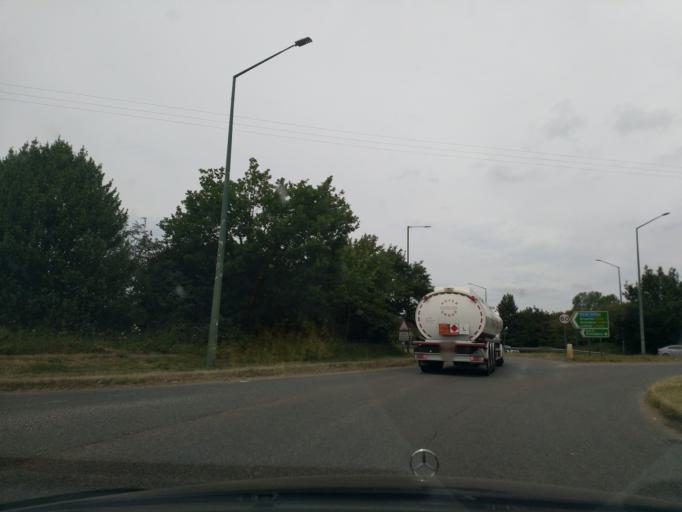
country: GB
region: England
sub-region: Solihull
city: Hampton in Arden
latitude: 52.4331
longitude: -1.6754
